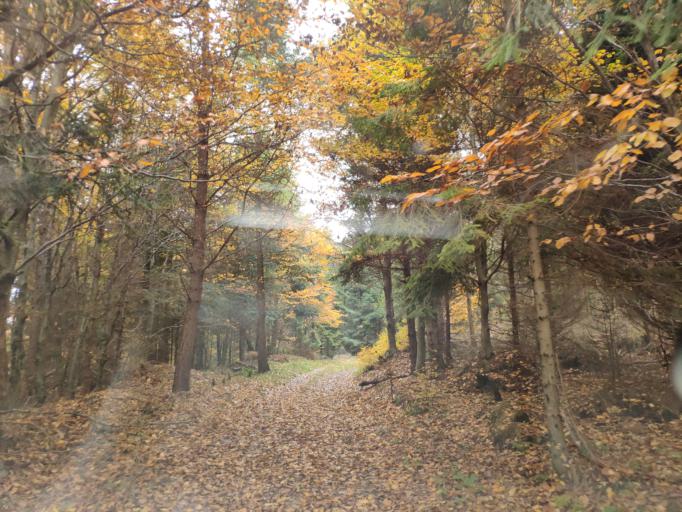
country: SK
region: Kosicky
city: Medzev
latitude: 48.7403
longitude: 20.9916
